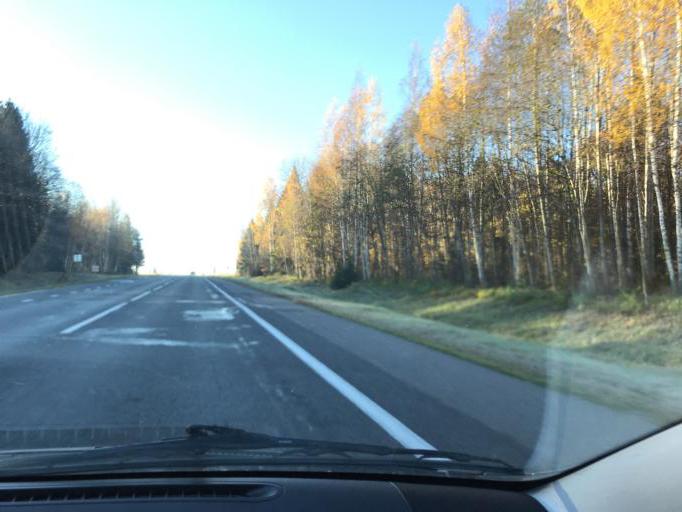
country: BY
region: Vitebsk
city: Vitebsk
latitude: 54.9139
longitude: 30.3754
